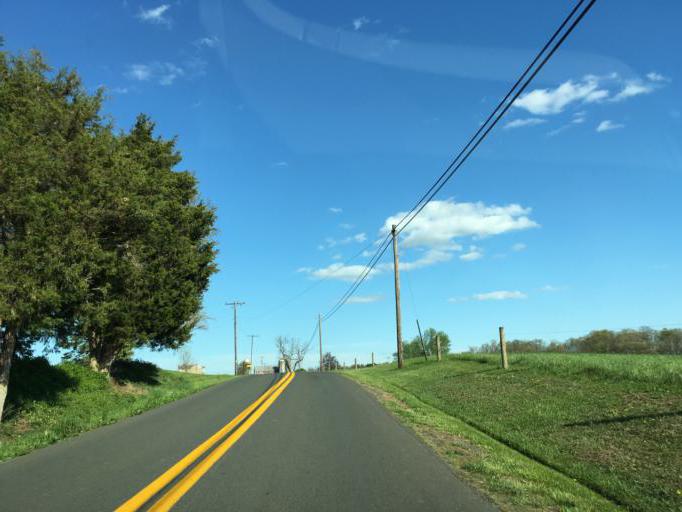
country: US
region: Maryland
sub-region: Frederick County
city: Woodsboro
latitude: 39.6211
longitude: -77.2809
